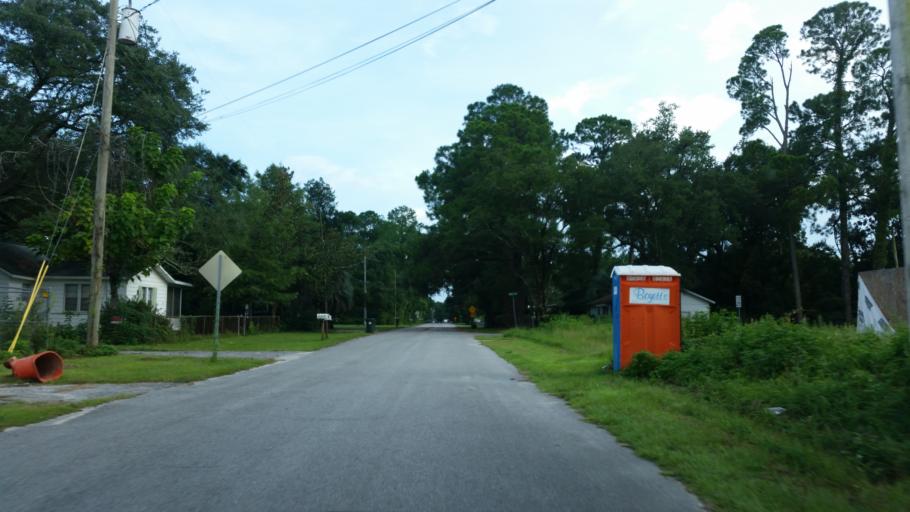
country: US
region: Florida
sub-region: Escambia County
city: Ferry Pass
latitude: 30.5152
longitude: -87.2127
